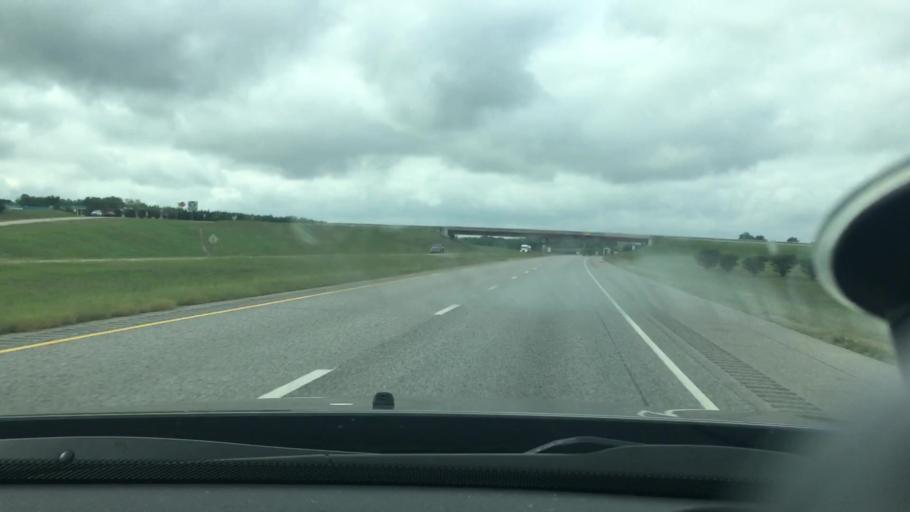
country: US
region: Oklahoma
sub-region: Bryan County
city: Durant
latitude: 34.1347
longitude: -96.2721
